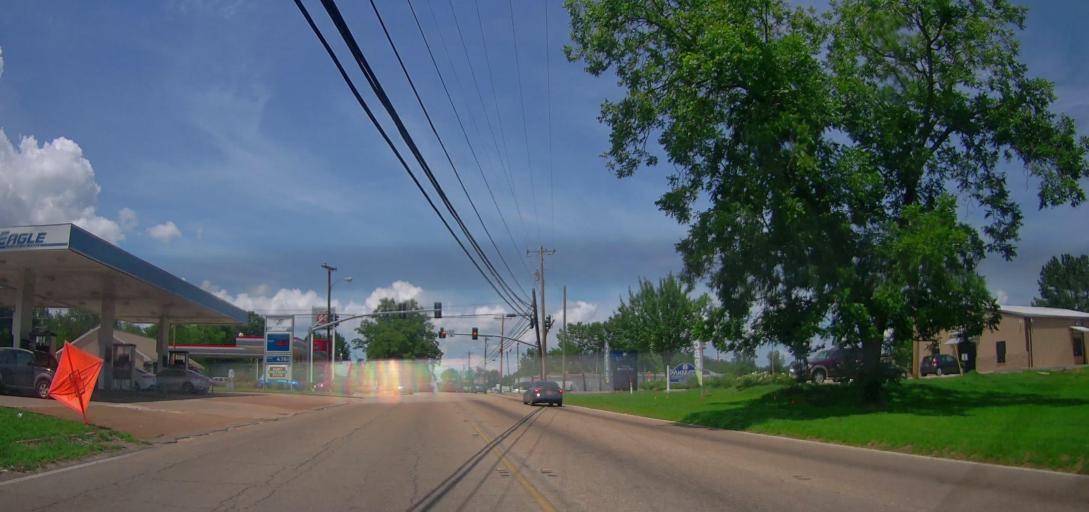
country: US
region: Mississippi
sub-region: Lee County
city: Verona
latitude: 34.1912
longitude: -88.7199
